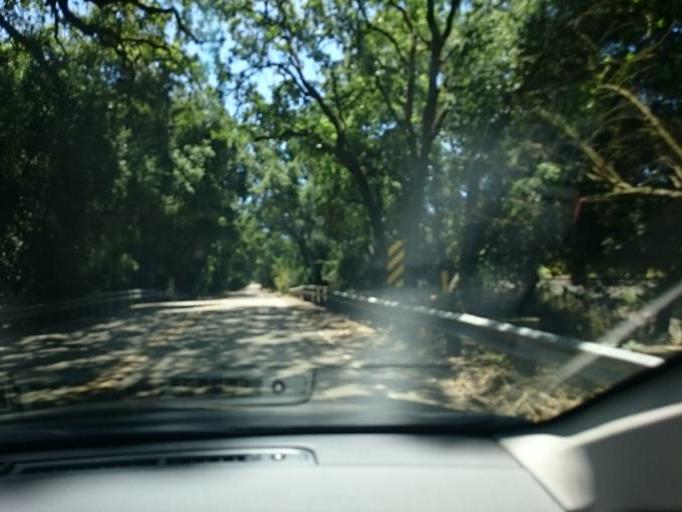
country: US
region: California
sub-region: San Joaquin County
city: Thornton
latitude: 38.2082
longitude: -121.4093
